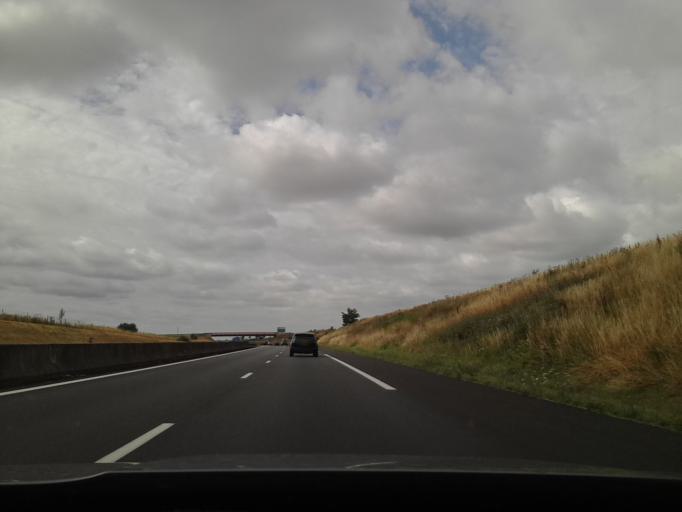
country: FR
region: Lower Normandy
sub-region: Departement de l'Orne
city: Sees
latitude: 48.6258
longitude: 0.1934
